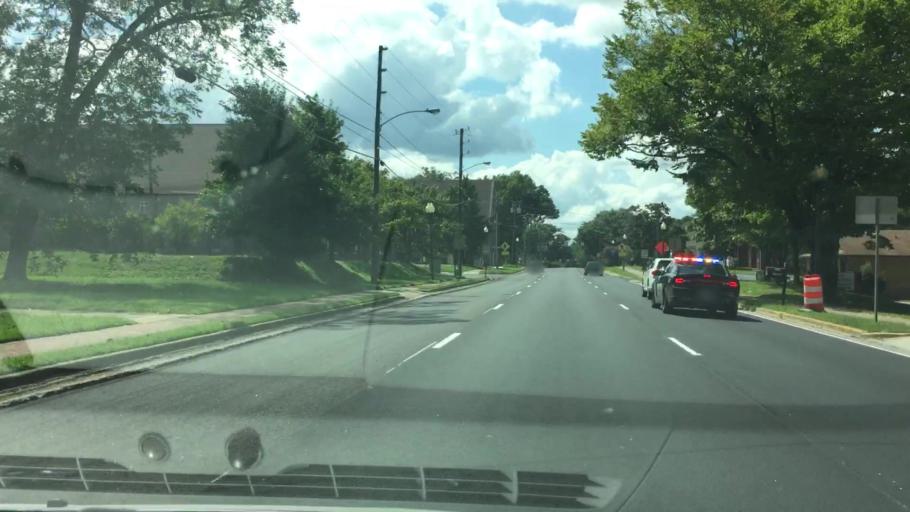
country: US
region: Georgia
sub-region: Fayette County
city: Fayetteville
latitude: 33.4487
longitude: -84.4516
